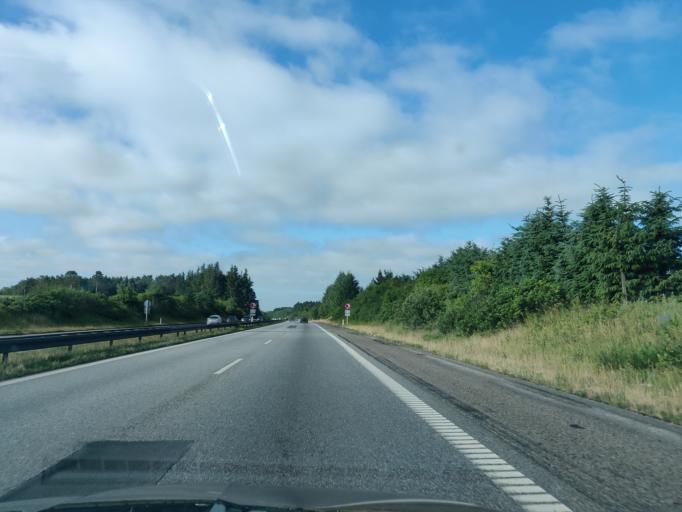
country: DK
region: North Denmark
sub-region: Alborg Kommune
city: Svenstrup
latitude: 56.9342
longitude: 9.8510
